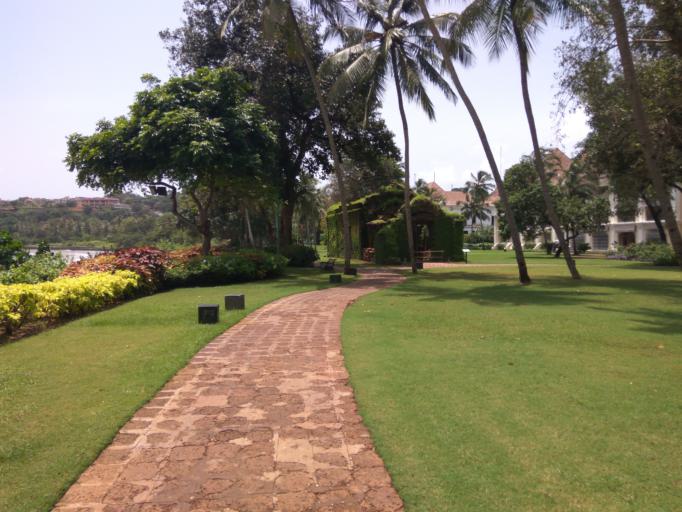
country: IN
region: Goa
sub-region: North Goa
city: Bambolim
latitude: 15.4510
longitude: 73.8507
